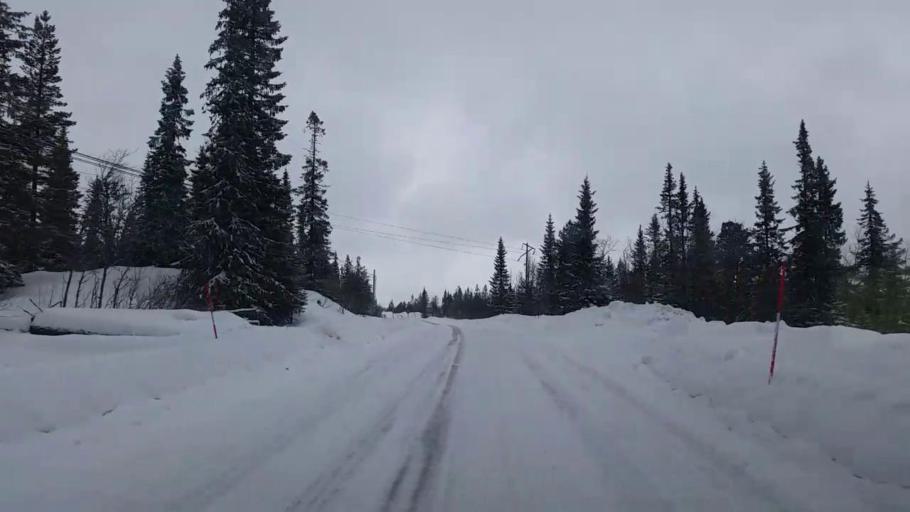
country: SE
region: Jaemtland
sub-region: Bergs Kommun
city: Hoverberg
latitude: 62.4911
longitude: 14.1172
